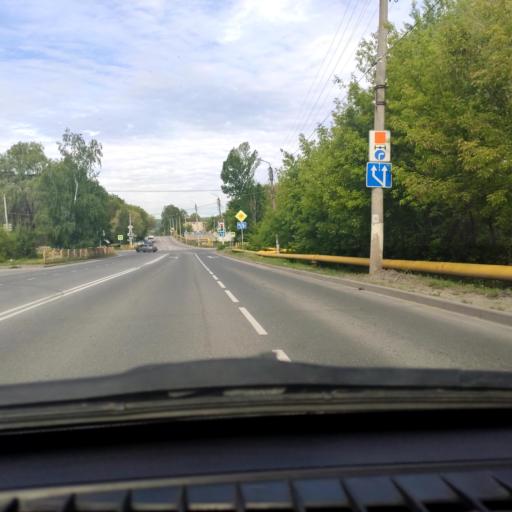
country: RU
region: Samara
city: Zhigulevsk
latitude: 53.4033
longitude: 49.5121
